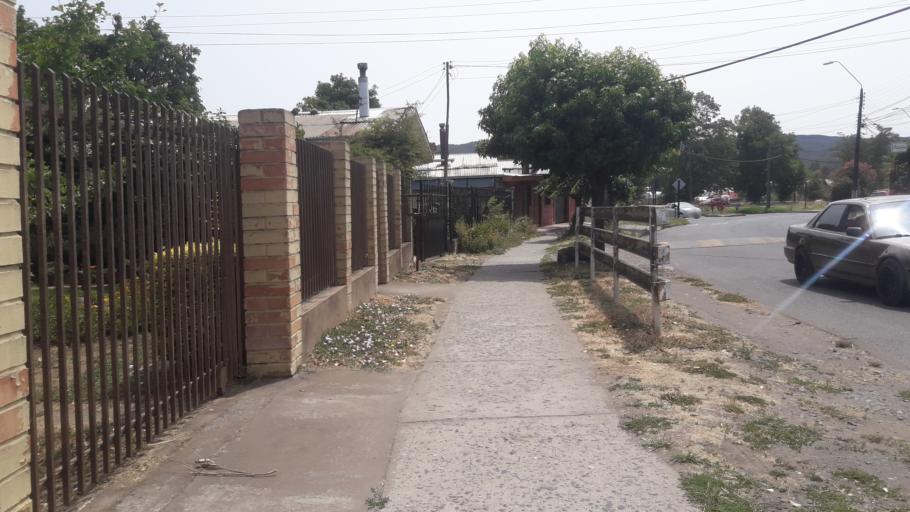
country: CL
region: Biobio
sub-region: Provincia de Biobio
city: Nacimiento
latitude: -37.5049
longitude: -72.6819
